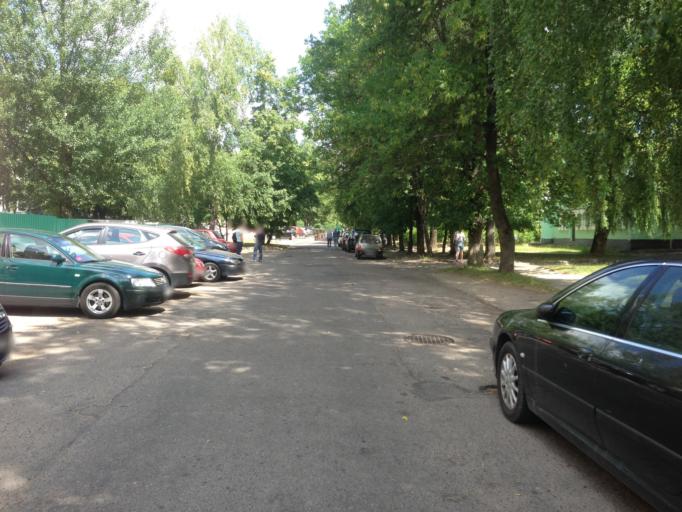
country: BY
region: Grodnenskaya
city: Hrodna
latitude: 53.6993
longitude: 23.8112
